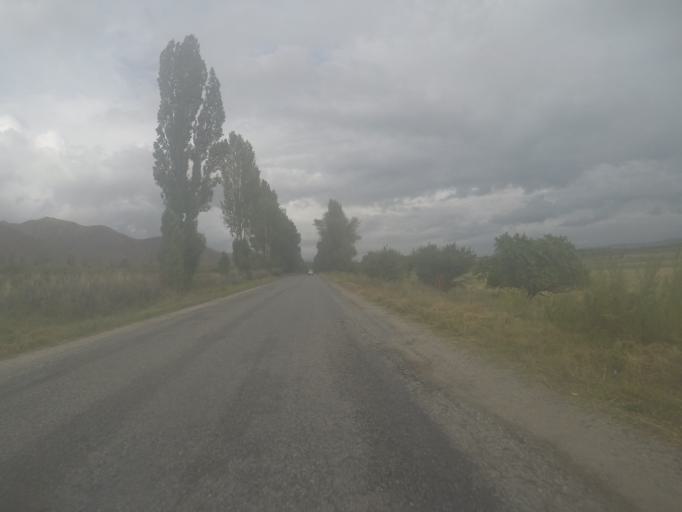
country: KG
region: Ysyk-Koel
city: Tyup
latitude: 42.7427
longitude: 78.0654
